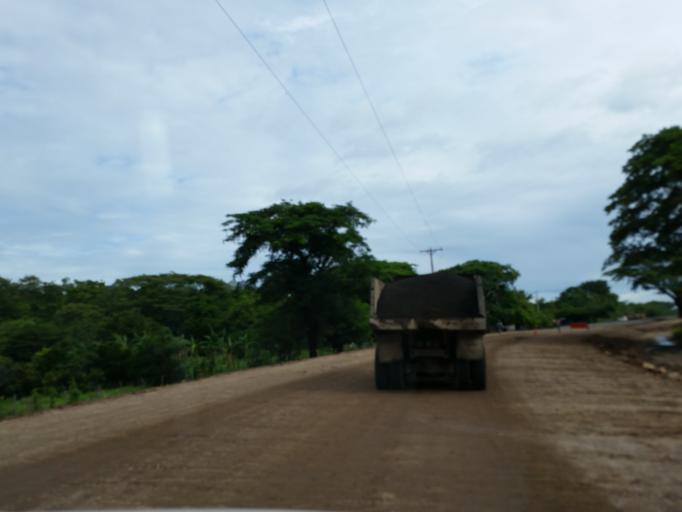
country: NI
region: Leon
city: La Paz Centro
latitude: 12.3876
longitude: -86.6635
